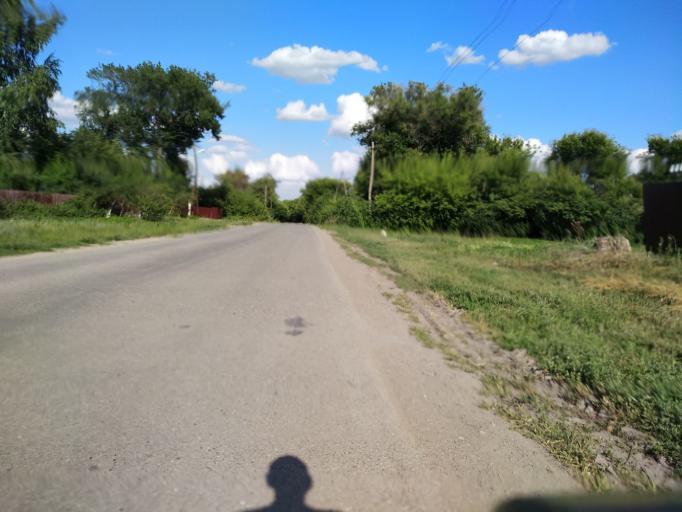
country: RU
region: Lipetsk
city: Dobrinka
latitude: 52.0394
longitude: 40.5462
